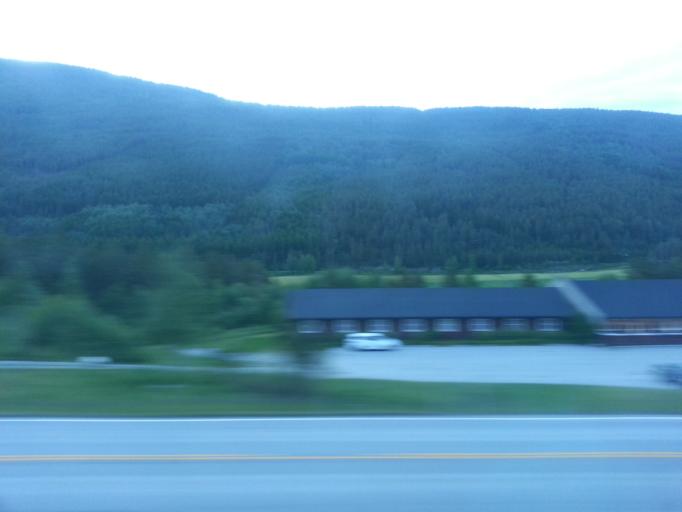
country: NO
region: Oppland
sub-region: Dovre
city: Dovre
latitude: 61.9120
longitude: 9.3594
